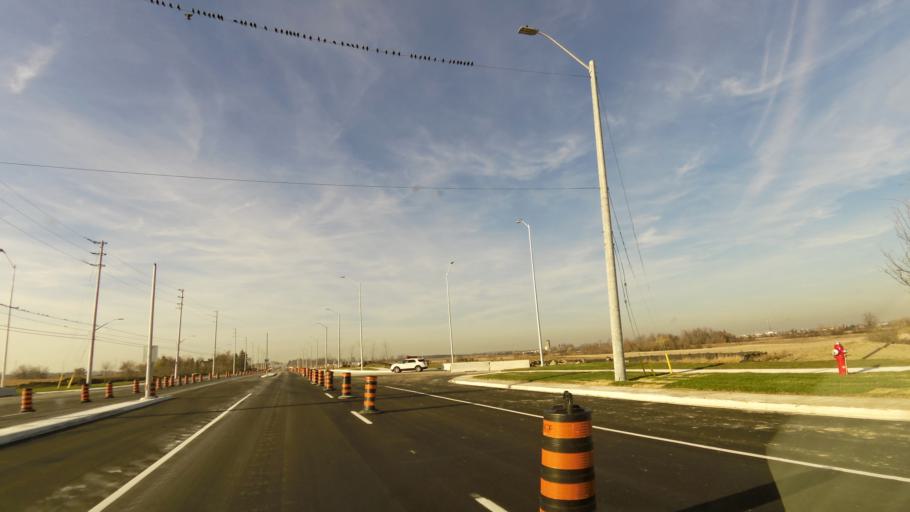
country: CA
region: Ontario
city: Brampton
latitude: 43.7783
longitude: -79.7662
